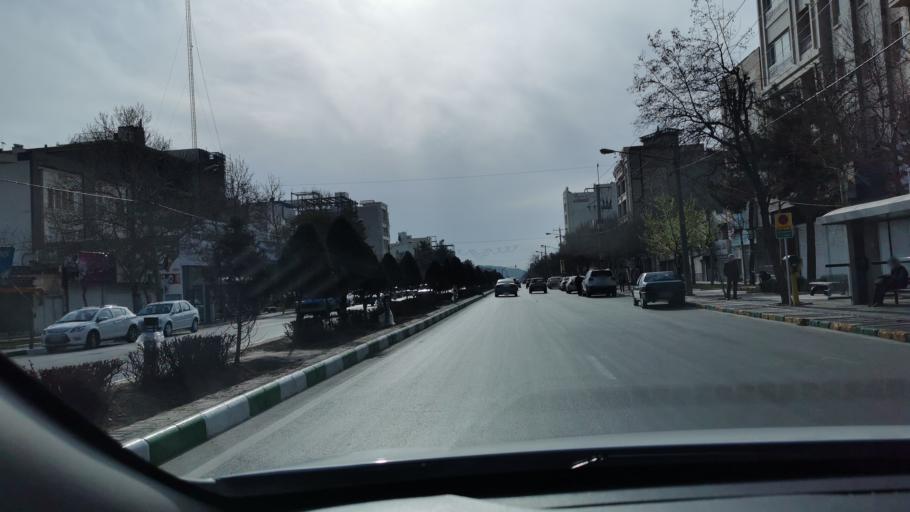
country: IR
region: Razavi Khorasan
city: Mashhad
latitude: 36.2907
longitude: 59.5382
